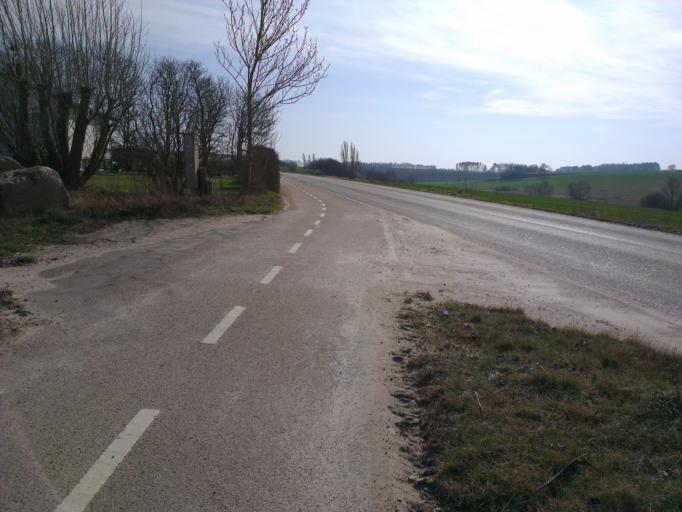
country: DK
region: Capital Region
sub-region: Frederikssund Kommune
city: Skibby
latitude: 55.8041
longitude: 11.8949
